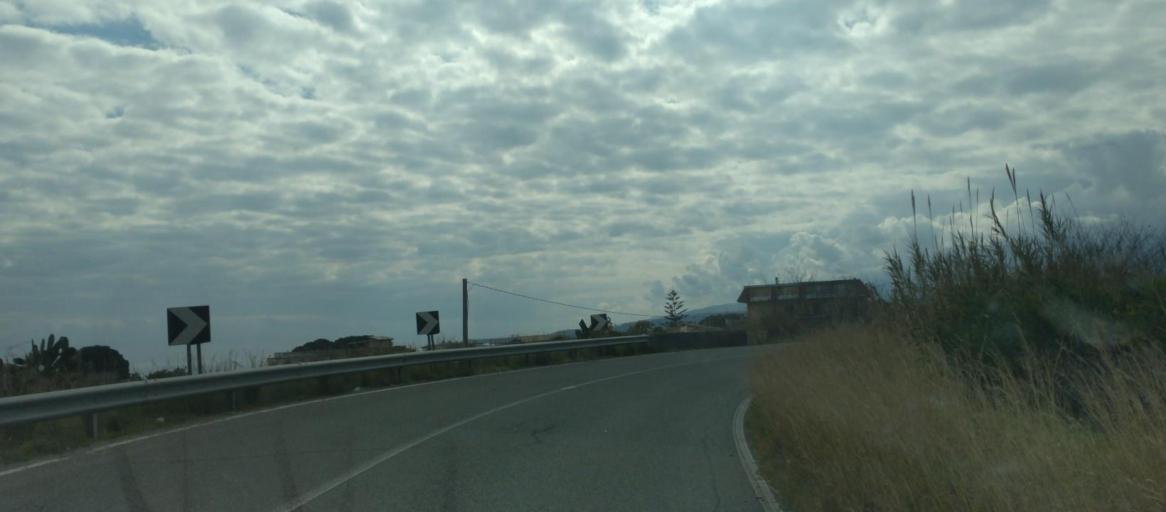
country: IT
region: Calabria
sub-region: Provincia di Catanzaro
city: Montepaone Lido
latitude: 38.7339
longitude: 16.5452
